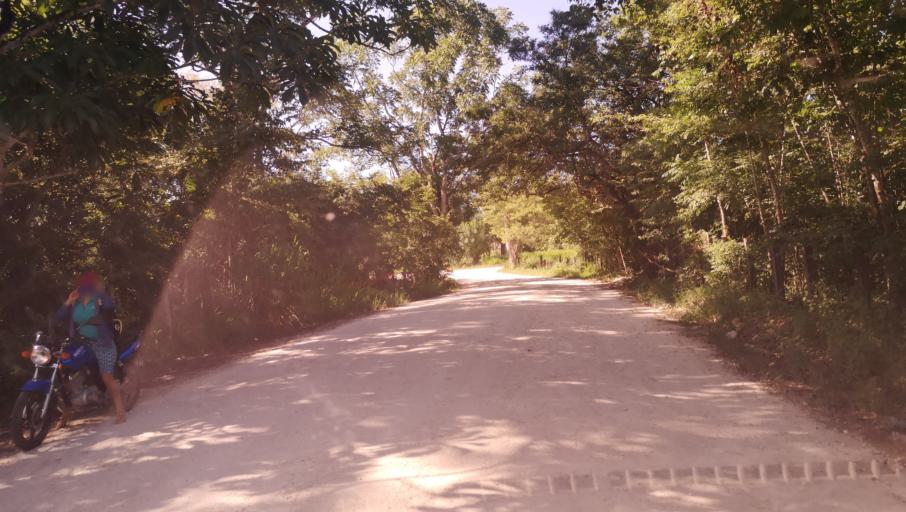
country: GT
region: Peten
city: Dolores
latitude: 16.7229
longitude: -89.3567
